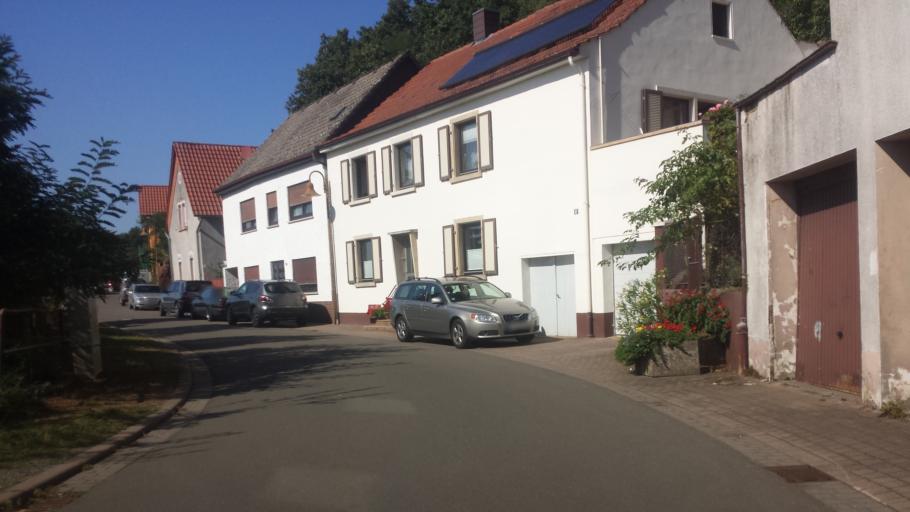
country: DE
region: Rheinland-Pfalz
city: Ramsen
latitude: 49.5531
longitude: 8.0265
